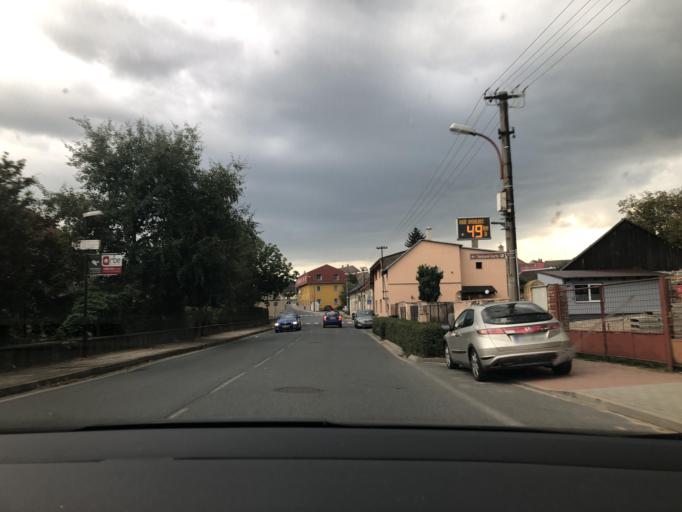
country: CZ
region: Central Bohemia
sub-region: Okres Kolin
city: Tynec nad Labem
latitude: 50.0456
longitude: 15.3610
